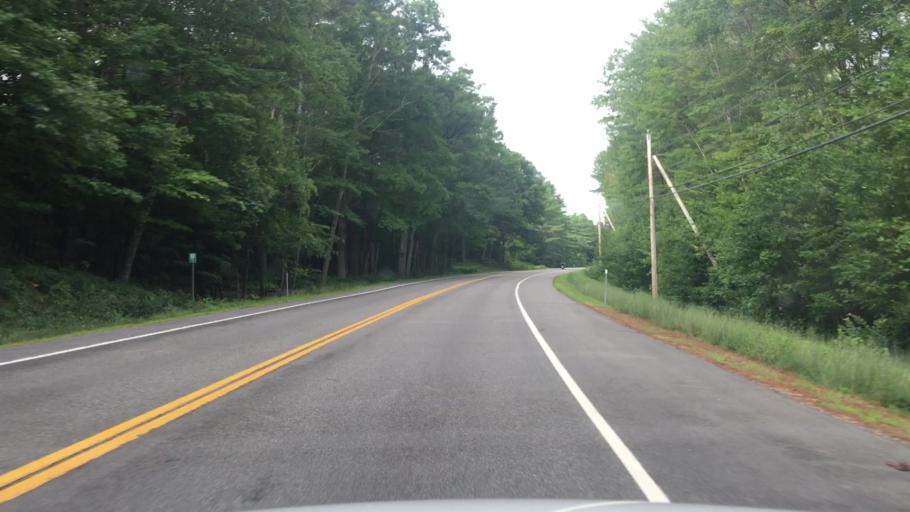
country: US
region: New Hampshire
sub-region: Carroll County
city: Sandwich
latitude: 43.8240
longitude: -71.3394
